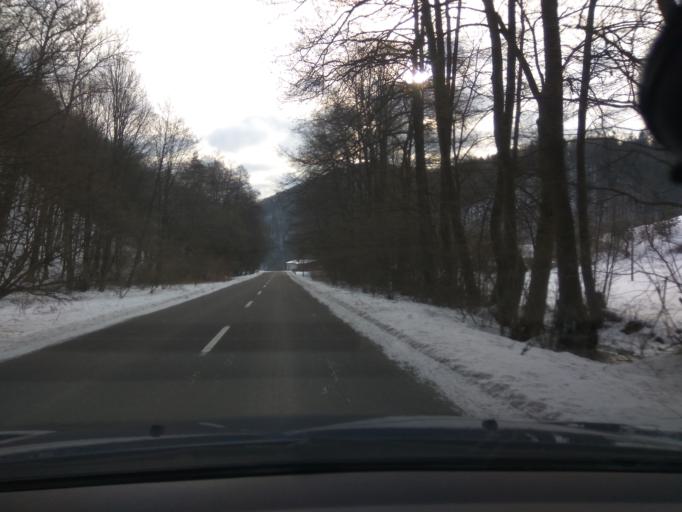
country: SK
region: Banskobystricky
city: Nova Bana
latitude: 48.5182
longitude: 18.6003
